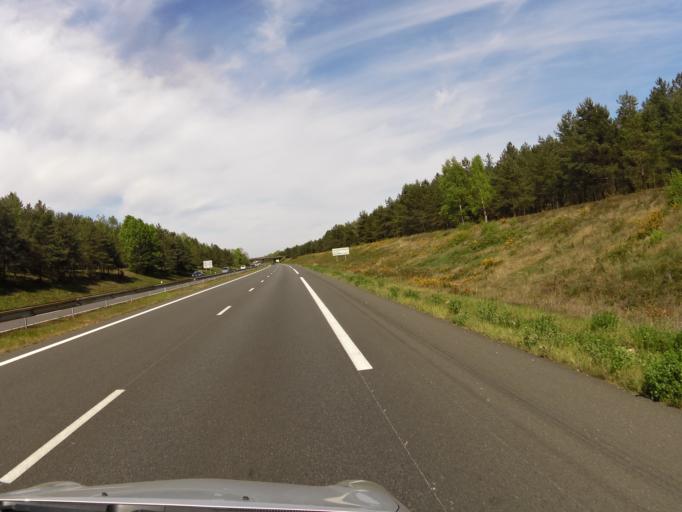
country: FR
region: Centre
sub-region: Departement du Loiret
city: Saint-Hilaire-Saint-Mesmin
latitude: 47.8181
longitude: 1.8577
